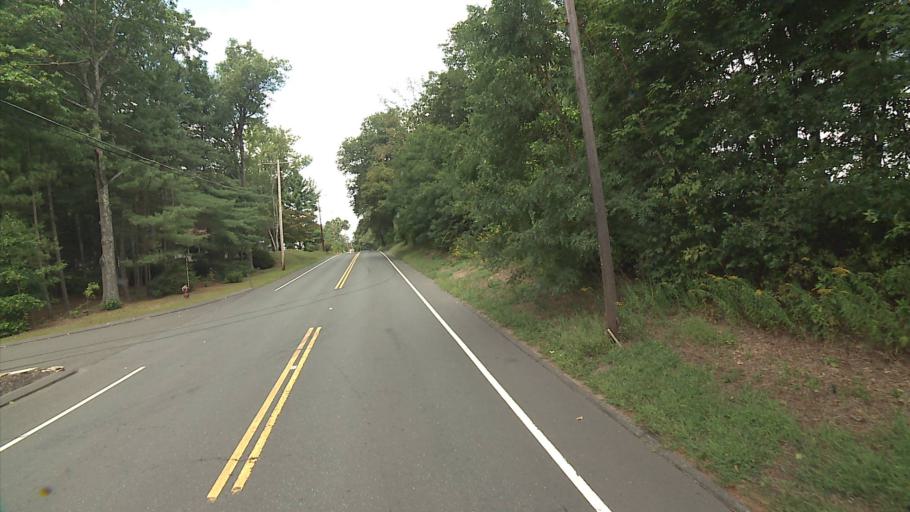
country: US
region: Connecticut
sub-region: Hartford County
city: Tariffville
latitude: 41.9361
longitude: -72.7709
